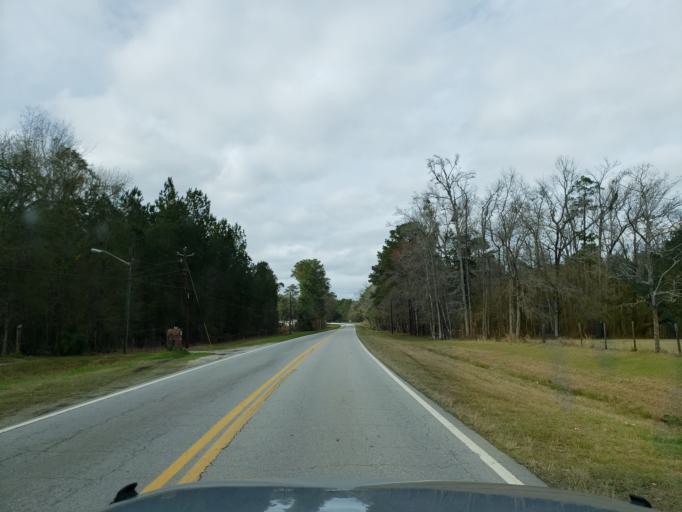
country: US
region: Georgia
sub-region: Chatham County
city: Georgetown
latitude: 32.0429
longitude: -81.2795
